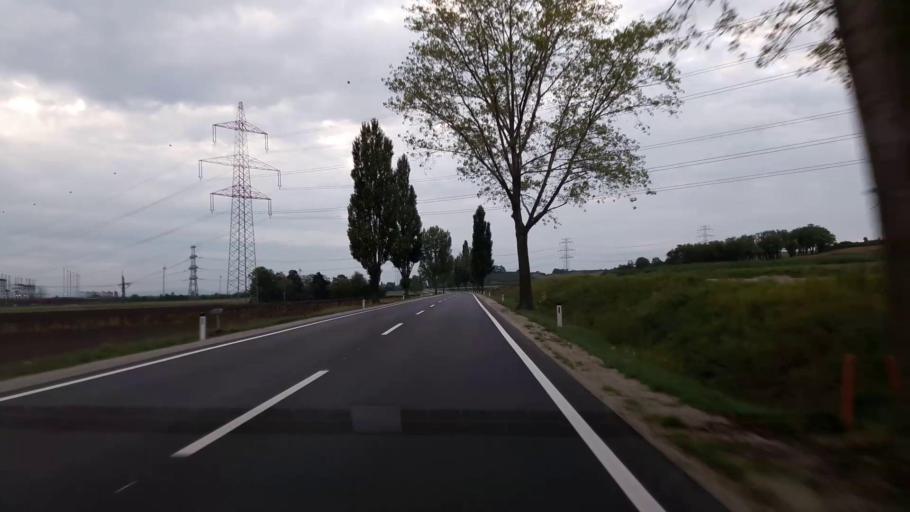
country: AT
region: Lower Austria
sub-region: Politischer Bezirk Bruck an der Leitha
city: Bruck an der Leitha
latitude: 48.0330
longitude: 16.7055
